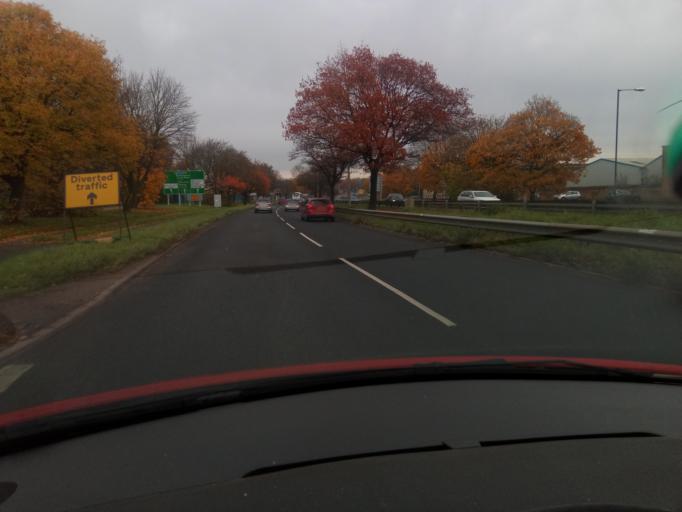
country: GB
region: England
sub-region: Derbyshire
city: Borrowash
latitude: 52.9112
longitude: -1.4289
